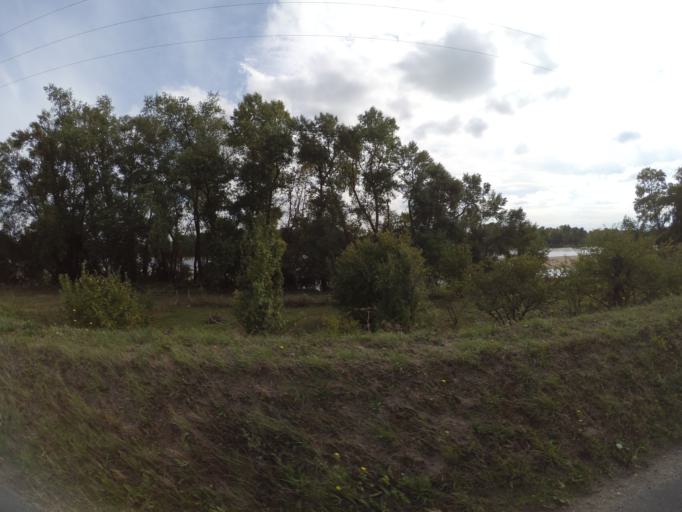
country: FR
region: Centre
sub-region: Departement d'Indre-et-Loire
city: Villandry
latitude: 47.3590
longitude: 0.4909
